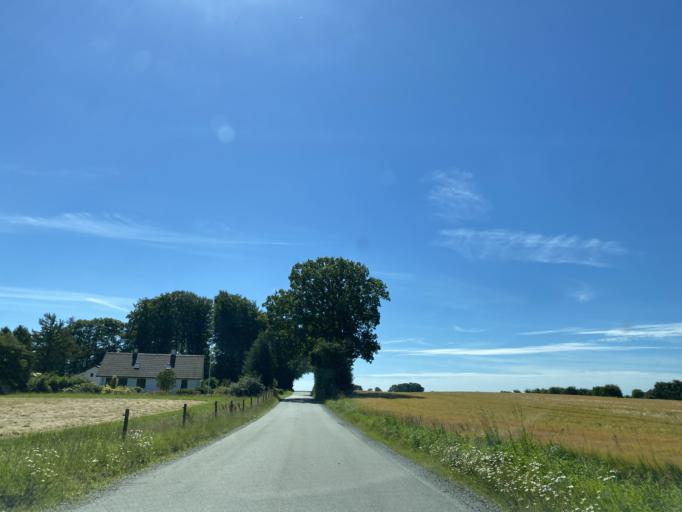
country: DK
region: South Denmark
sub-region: Vejle Kommune
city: Vejle
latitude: 55.6357
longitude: 9.5402
